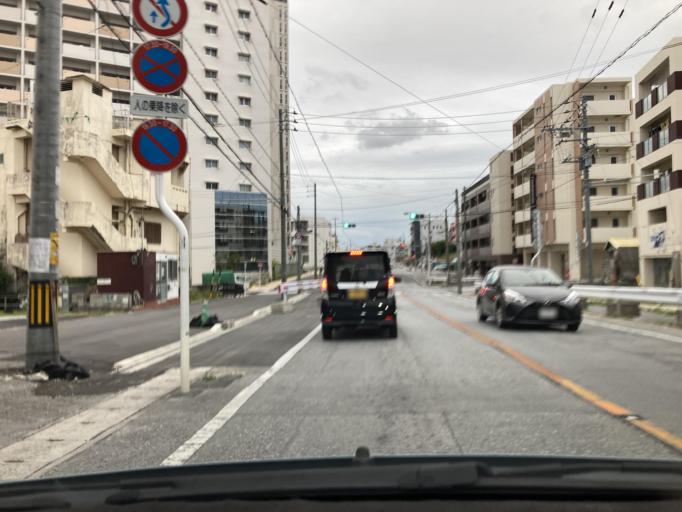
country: JP
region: Okinawa
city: Naha-shi
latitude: 26.2107
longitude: 127.6888
